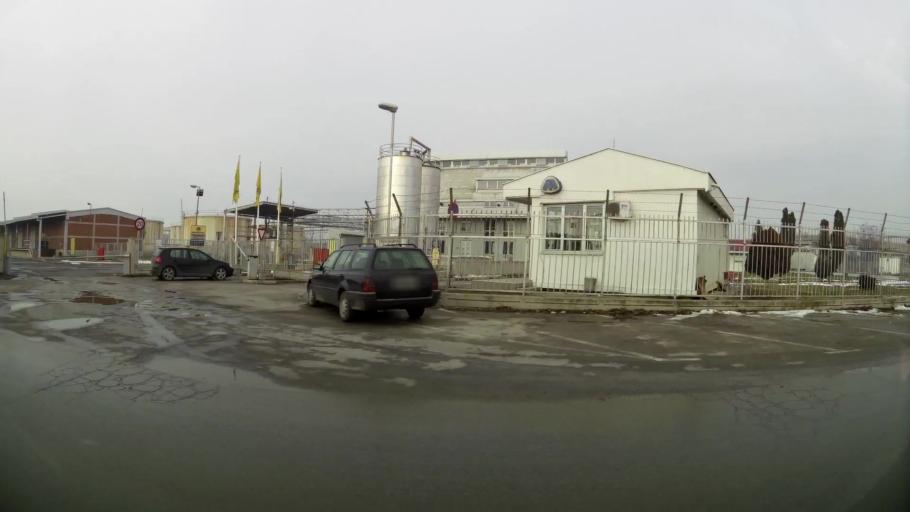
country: MK
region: Ilinden
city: Ilinden
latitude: 41.9974
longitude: 21.5724
